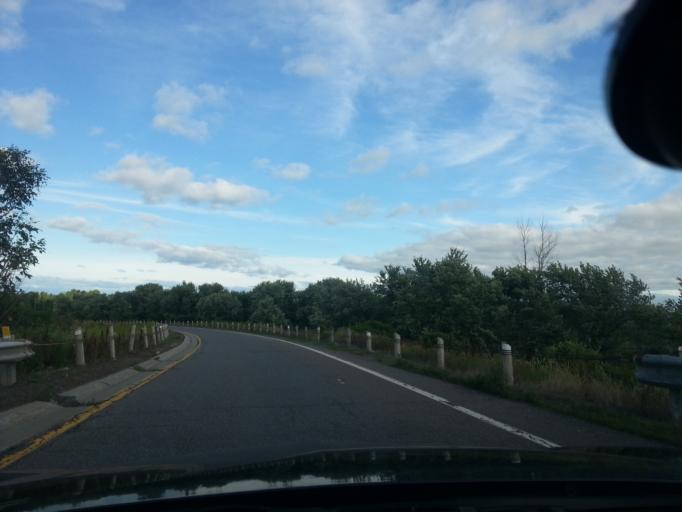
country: CA
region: Ontario
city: Hawkesbury
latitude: 45.5648
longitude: -74.5039
